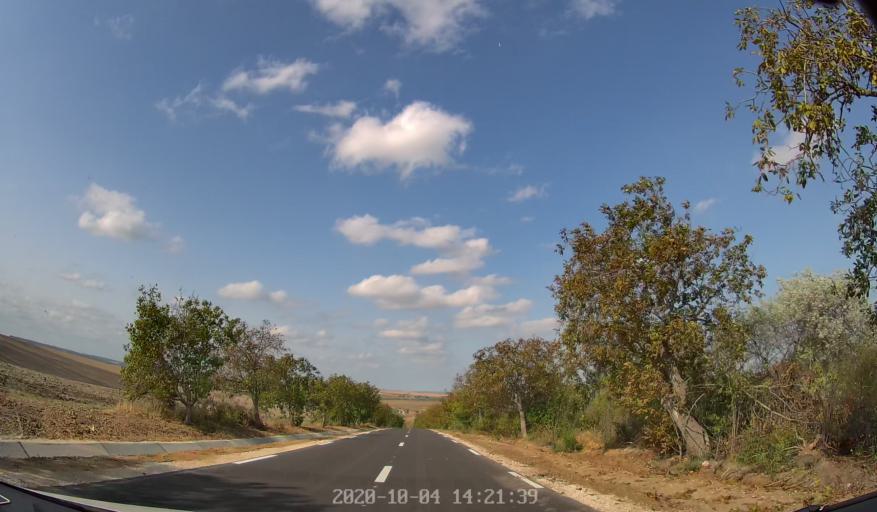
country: MD
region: Rezina
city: Saharna
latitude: 47.5875
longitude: 28.9544
